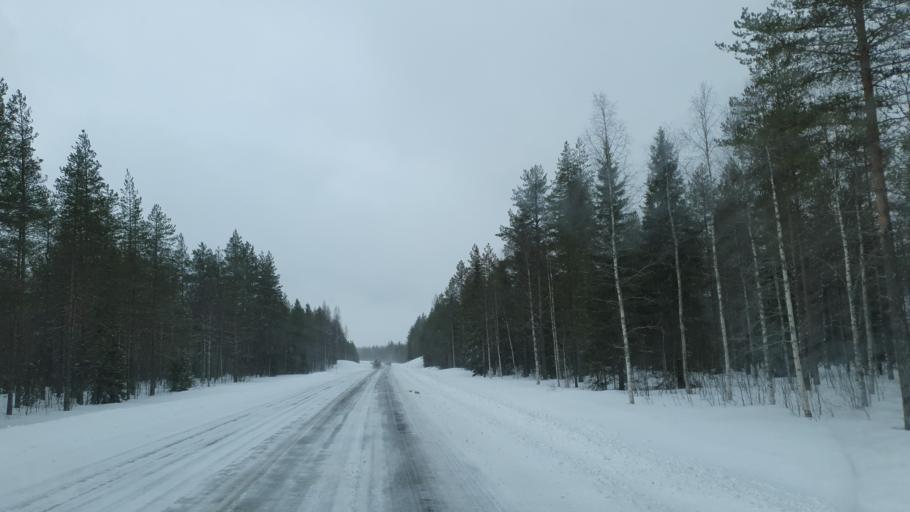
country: FI
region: Lapland
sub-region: Rovaniemi
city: Ranua
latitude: 66.0333
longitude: 26.3328
